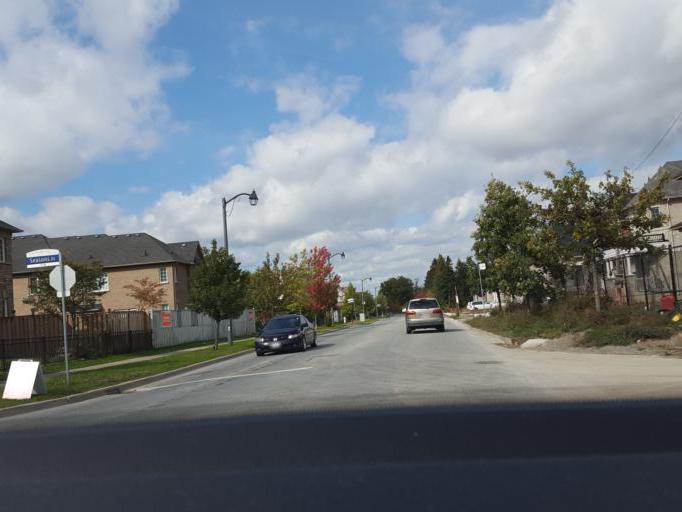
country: CA
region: Ontario
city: Markham
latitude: 43.8305
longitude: -79.2237
